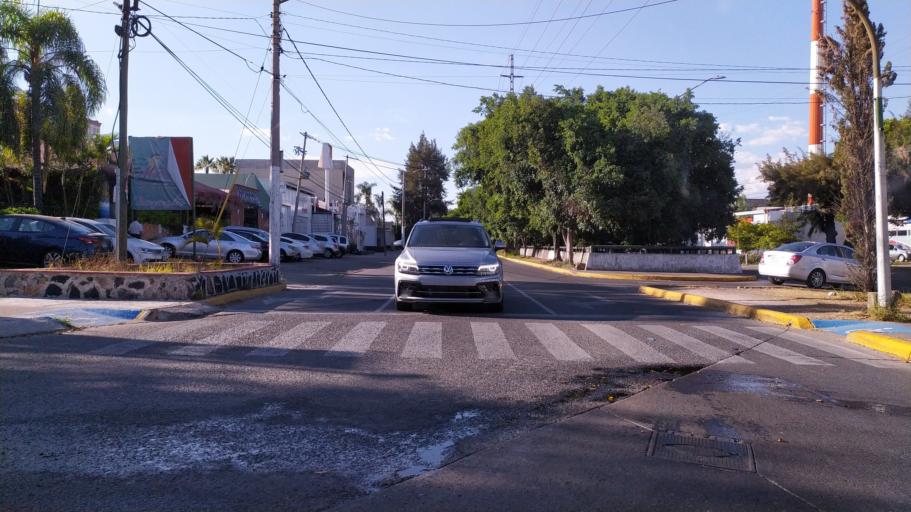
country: MX
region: Jalisco
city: Guadalajara
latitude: 20.6779
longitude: -103.4054
